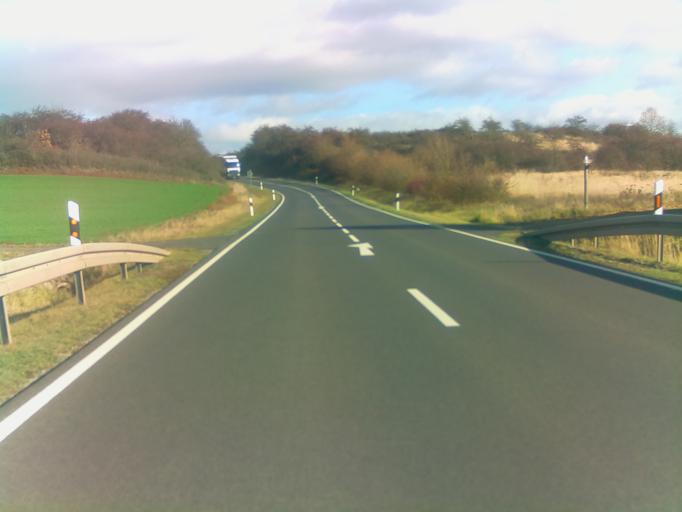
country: DE
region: Bavaria
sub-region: Regierungsbezirk Unterfranken
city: Trappstadt
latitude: 50.3336
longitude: 10.5835
